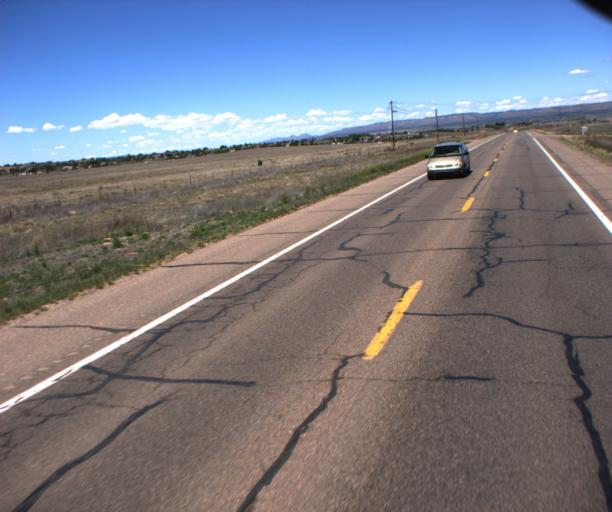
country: US
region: Arizona
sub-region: Yavapai County
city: Paulden
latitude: 34.8501
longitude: -112.4666
